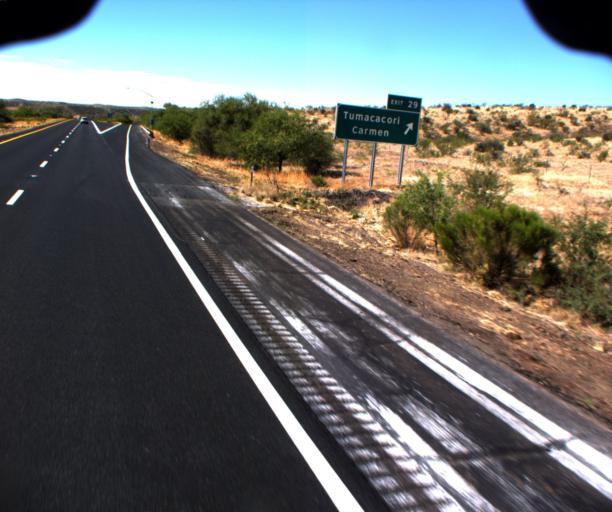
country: US
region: Arizona
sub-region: Santa Cruz County
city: Tubac
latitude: 31.5618
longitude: -111.0525
